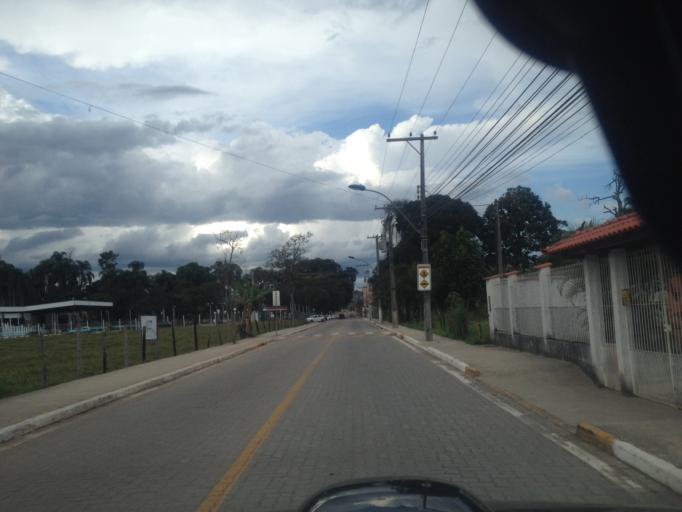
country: BR
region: Rio de Janeiro
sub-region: Porto Real
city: Porto Real
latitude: -22.4145
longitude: -44.2990
